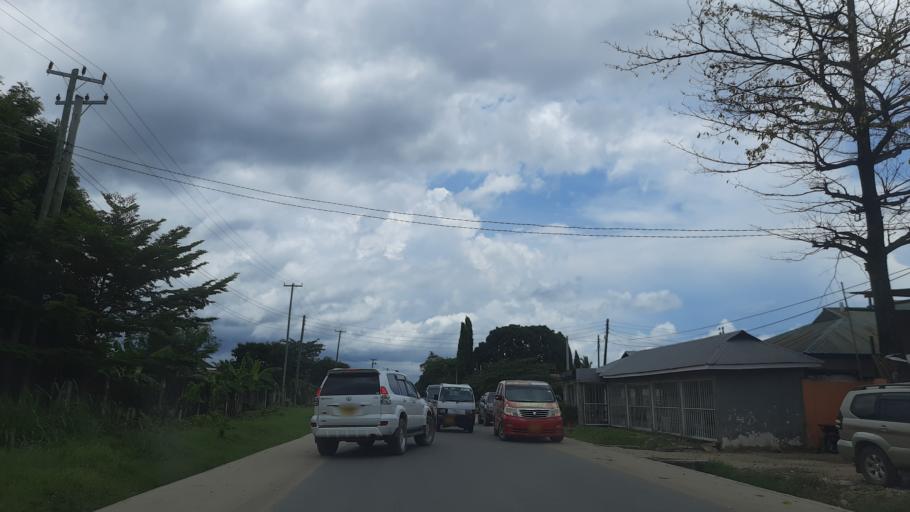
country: TZ
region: Dar es Salaam
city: Magomeni
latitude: -6.7782
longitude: 39.2367
